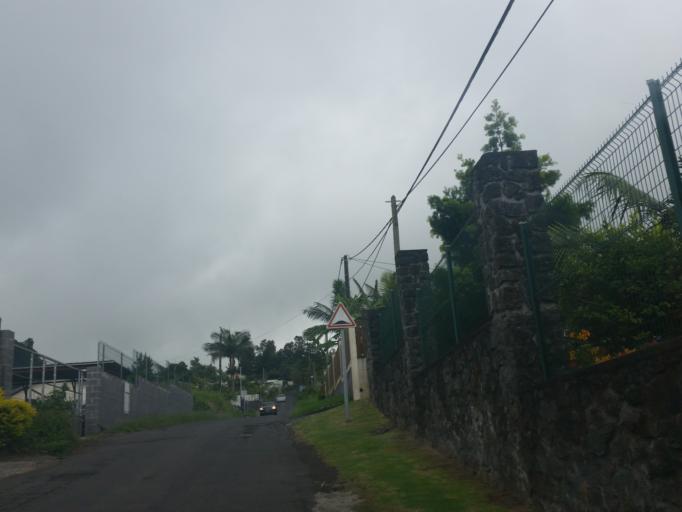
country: RE
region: Reunion
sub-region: Reunion
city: Le Tampon
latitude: -21.2322
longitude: 55.5224
